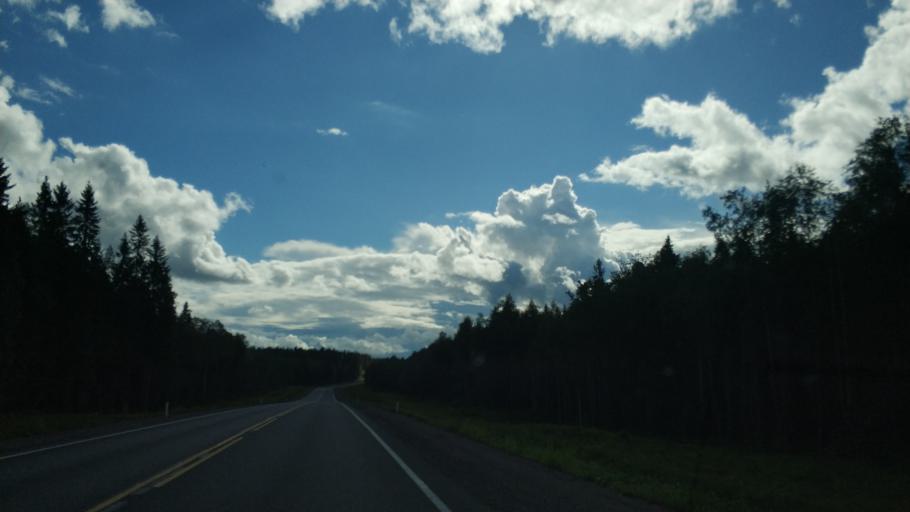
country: RU
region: Republic of Karelia
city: Ruskeala
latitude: 61.8607
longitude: 30.6521
